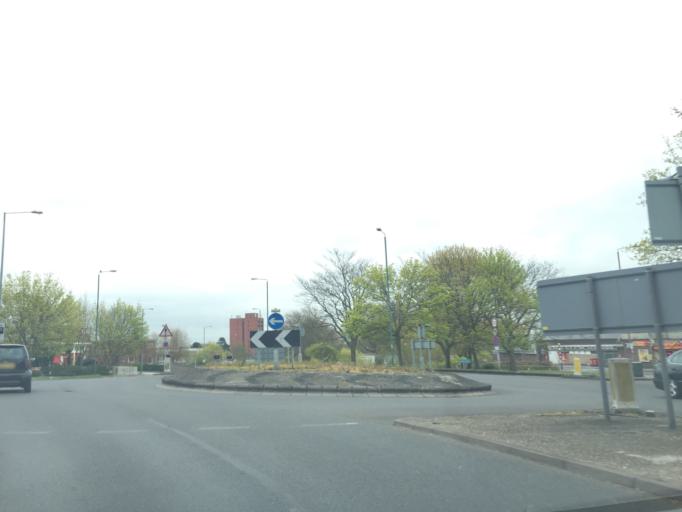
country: GB
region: England
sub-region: Essex
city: Harlow
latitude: 51.7716
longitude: 0.0914
